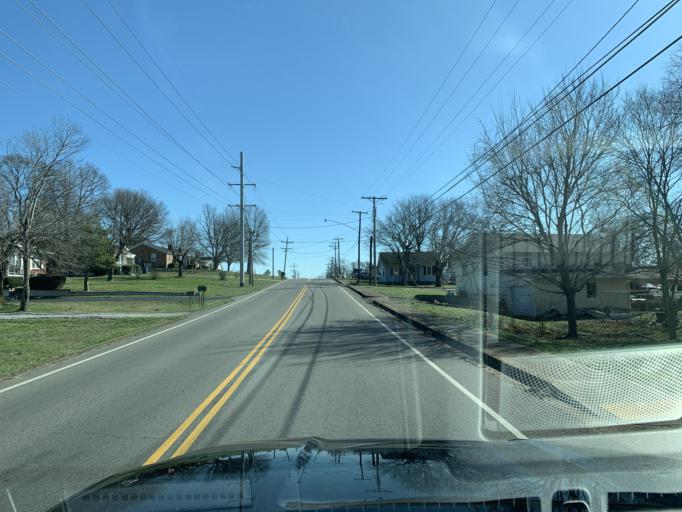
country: US
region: Tennessee
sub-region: Maury County
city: Mount Pleasant
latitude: 35.5421
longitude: -87.2157
